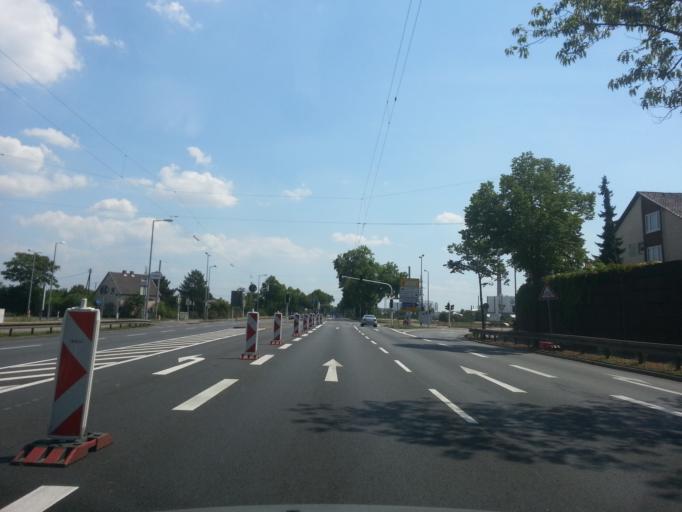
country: DE
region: Baden-Wuerttemberg
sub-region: Karlsruhe Region
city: Mannheim
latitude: 49.5458
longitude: 8.4561
